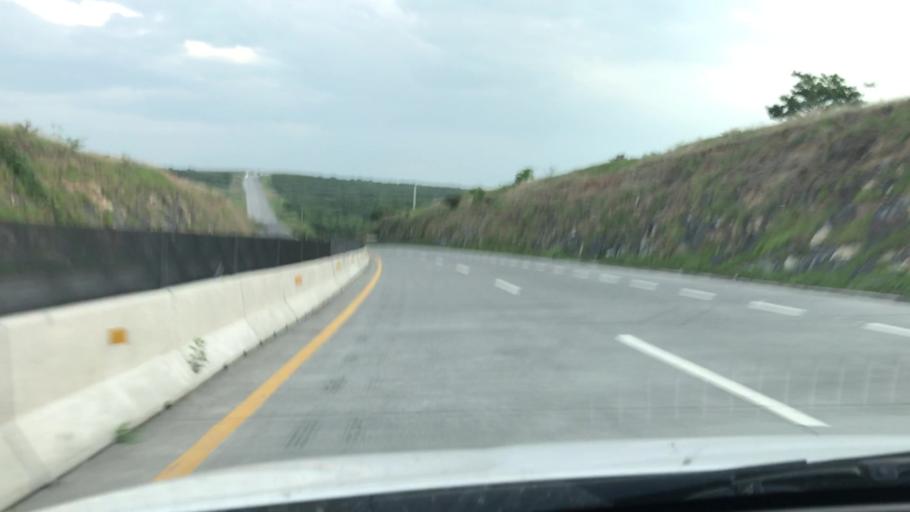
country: MX
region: Jalisco
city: Degollado
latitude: 20.3822
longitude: -102.1197
